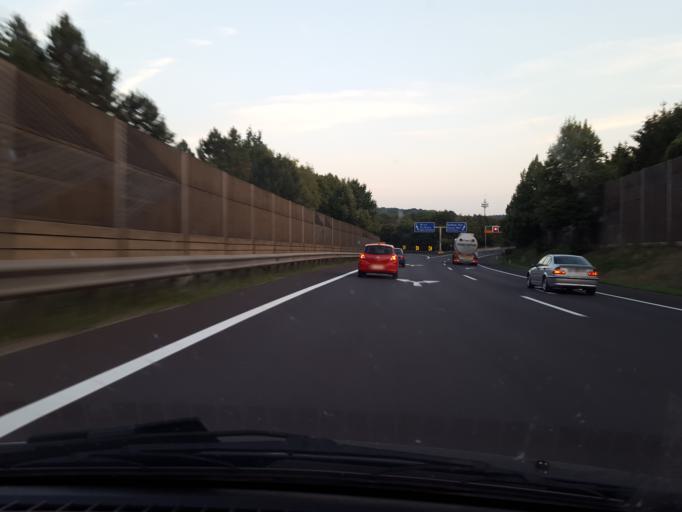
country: AT
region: Upper Austria
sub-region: Politischer Bezirk Linz-Land
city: Ansfelden
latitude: 48.2248
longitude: 14.2994
